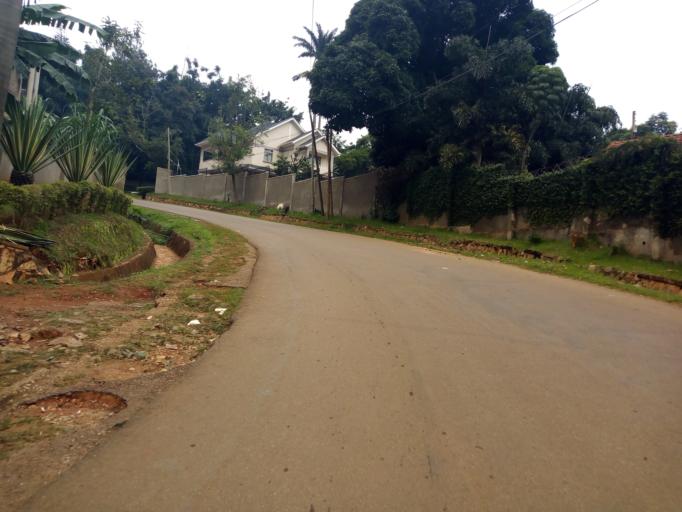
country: UG
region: Central Region
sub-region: Wakiso District
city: Kireka
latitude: 0.3250
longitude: 32.6259
